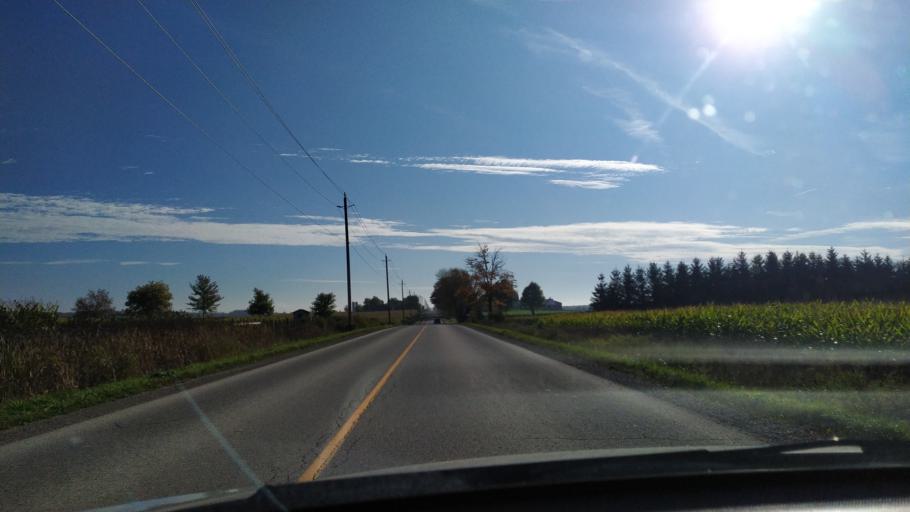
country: CA
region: Ontario
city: Waterloo
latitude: 43.4931
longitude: -80.7326
